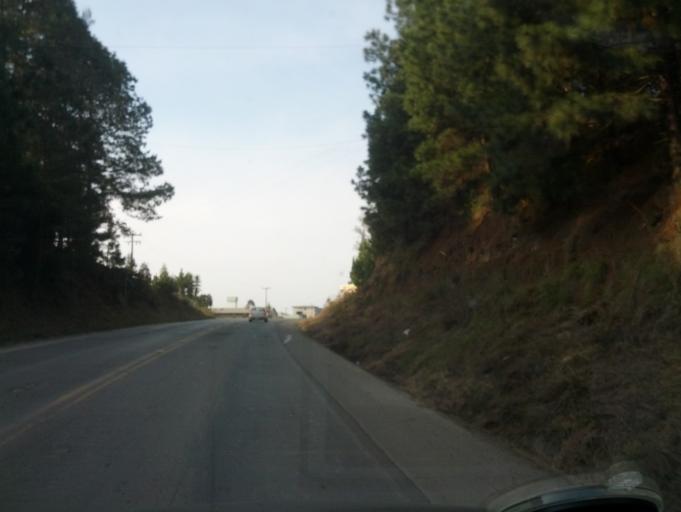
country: BR
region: Santa Catarina
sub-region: Otacilio Costa
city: Otacilio Costa
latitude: -27.5844
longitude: -50.1651
